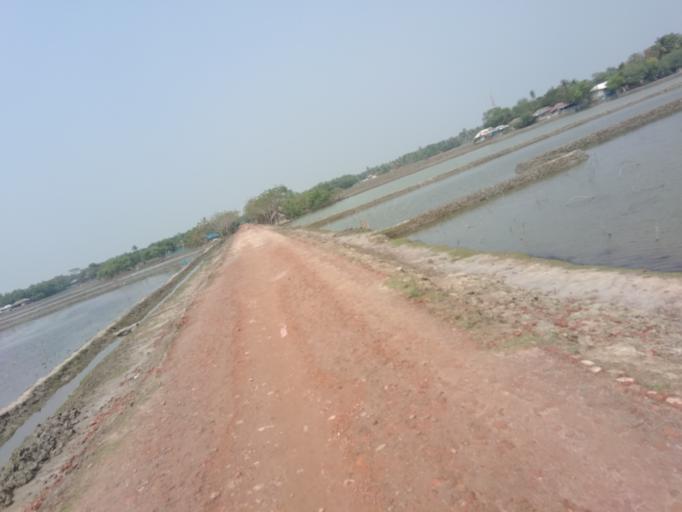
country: IN
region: West Bengal
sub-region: North 24 Parganas
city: Taki
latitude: 22.2941
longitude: 89.2704
